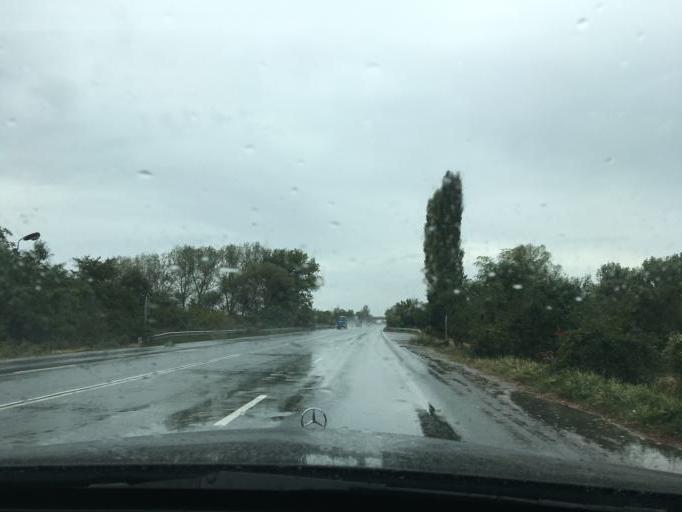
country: BG
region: Sofiya
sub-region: Obshtina Bozhurishte
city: Bozhurishte
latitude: 42.7950
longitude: 23.1464
